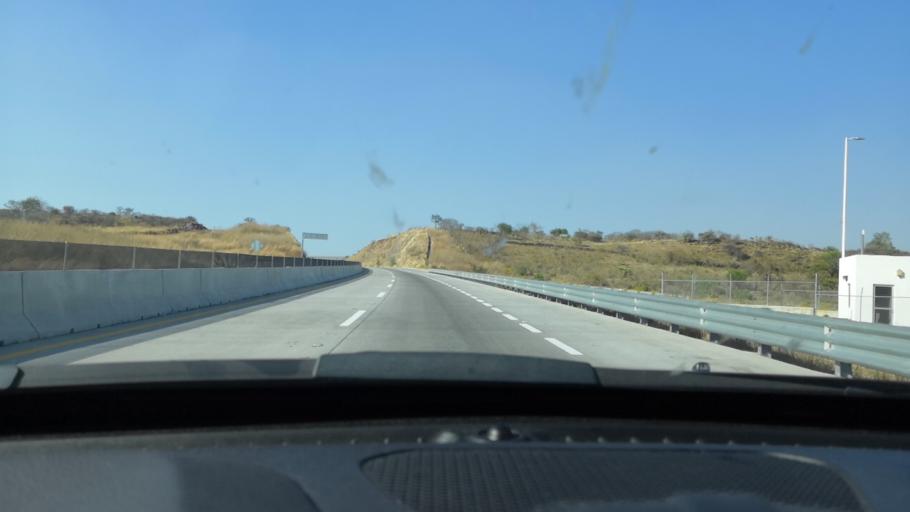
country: MX
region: Jalisco
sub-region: Zapotlanejo
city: La Mezquitera
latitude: 20.5879
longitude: -103.0990
